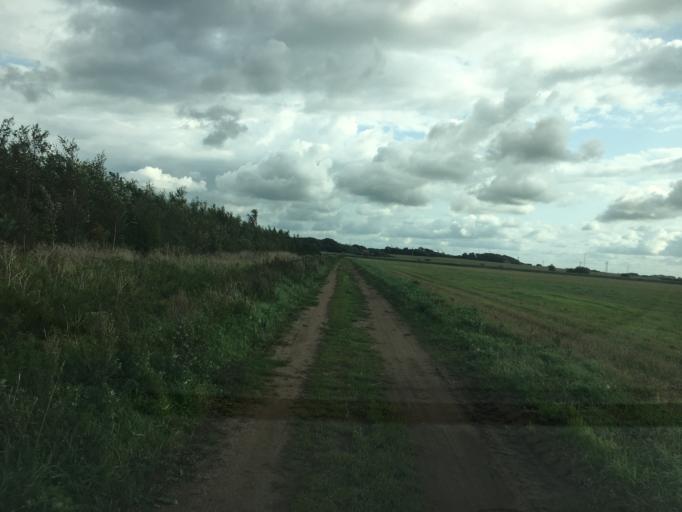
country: DK
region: South Denmark
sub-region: Tonder Kommune
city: Tonder
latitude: 54.9434
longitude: 8.9109
